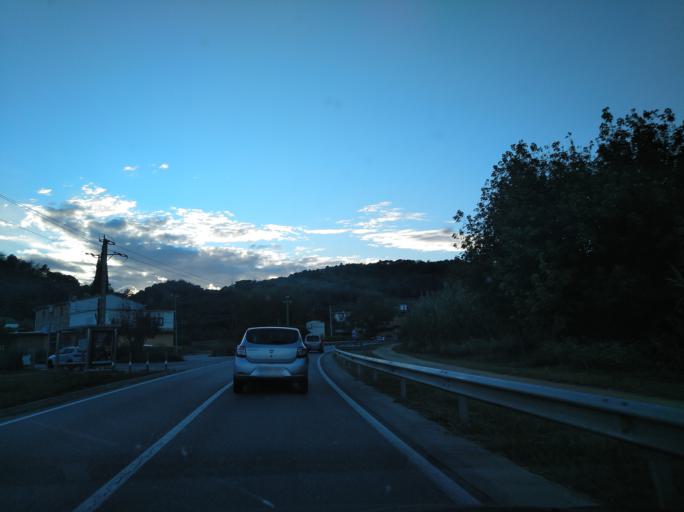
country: ES
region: Catalonia
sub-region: Provincia de Girona
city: Bescano
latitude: 41.9679
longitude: 2.7222
